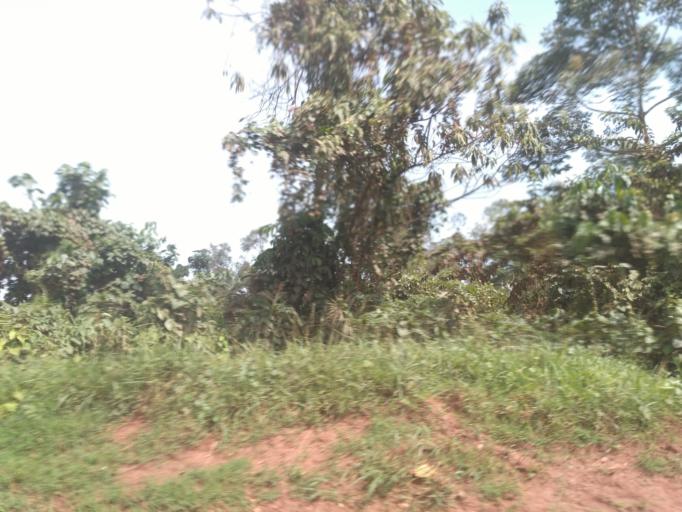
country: UG
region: Central Region
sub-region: Wakiso District
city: Kireka
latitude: 0.4412
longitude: 32.5901
